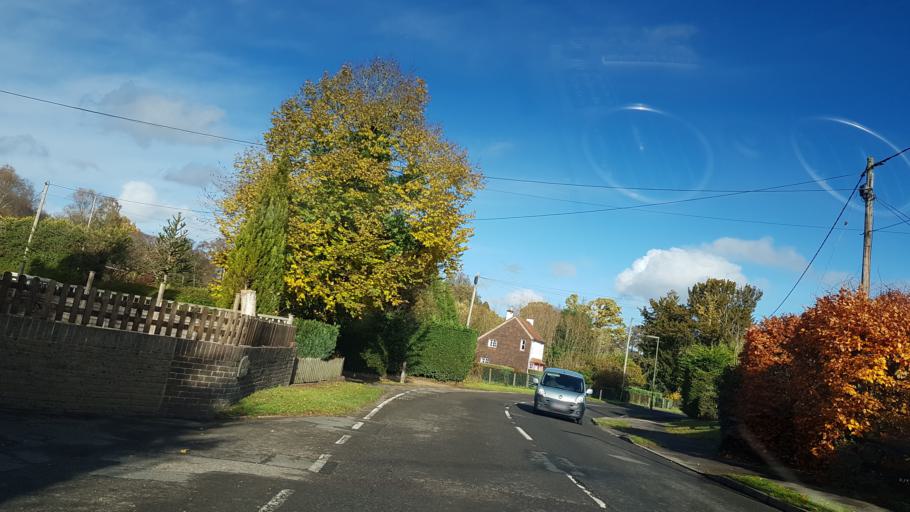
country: GB
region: England
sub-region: Surrey
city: Elstead
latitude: 51.1760
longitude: -0.7126
